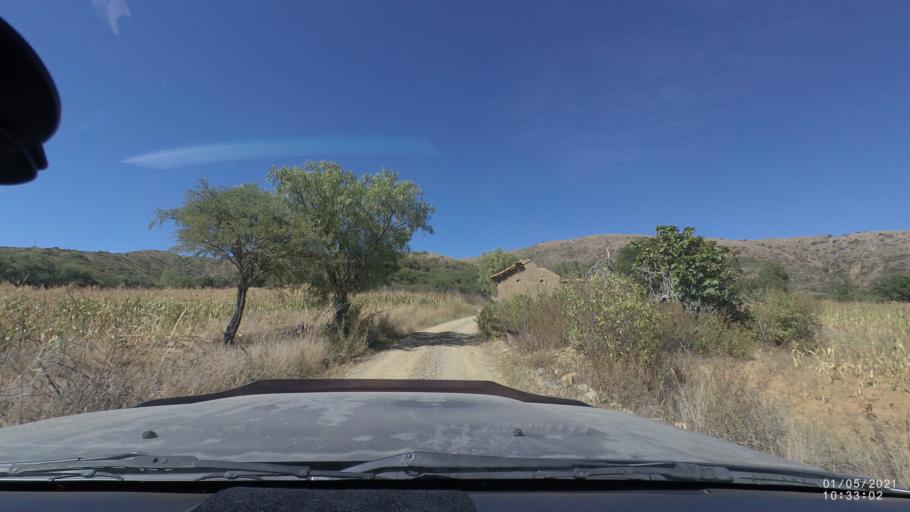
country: BO
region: Cochabamba
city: Capinota
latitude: -17.5957
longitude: -66.1941
